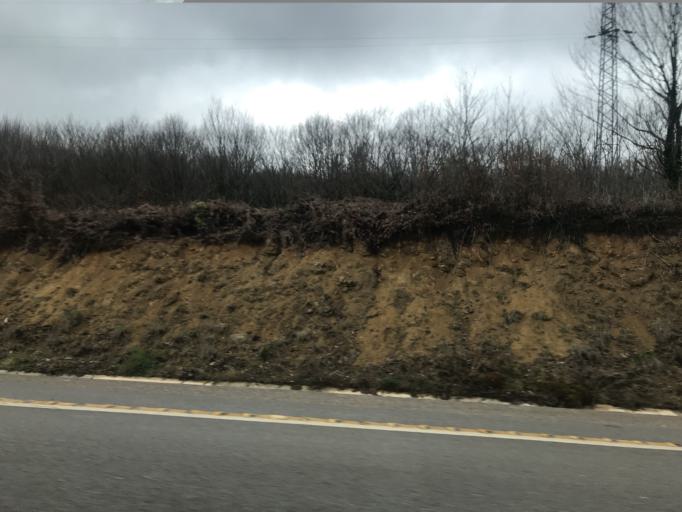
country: TR
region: Bartin
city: Amasra
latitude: 41.7164
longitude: 32.3949
